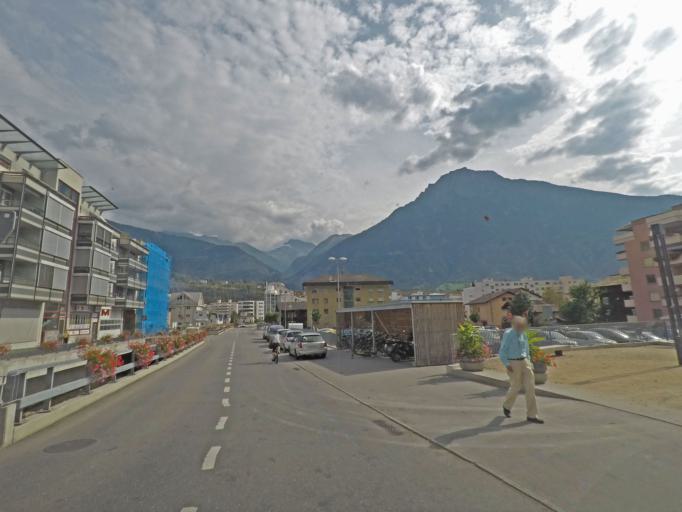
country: CH
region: Valais
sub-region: Brig District
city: Naters
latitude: 46.3252
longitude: 7.9896
